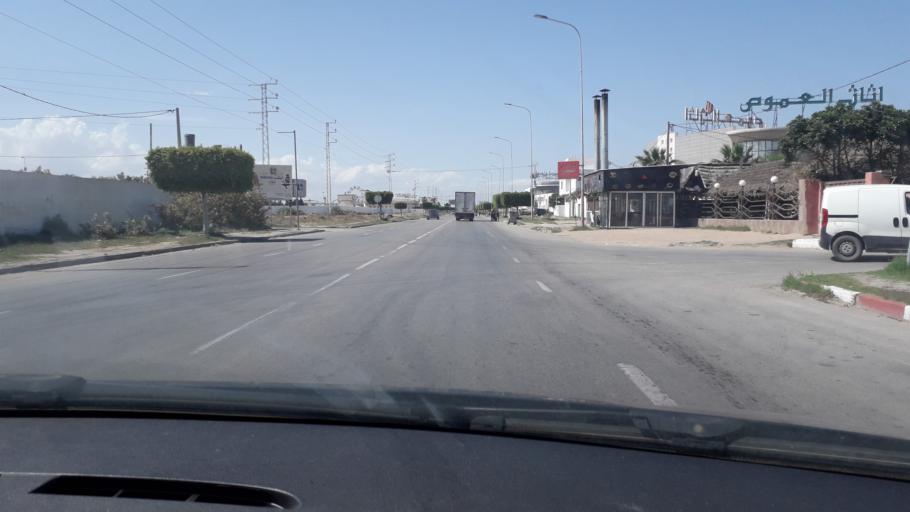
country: TN
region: Safaqis
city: Al Qarmadah
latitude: 34.8389
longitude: 10.7645
